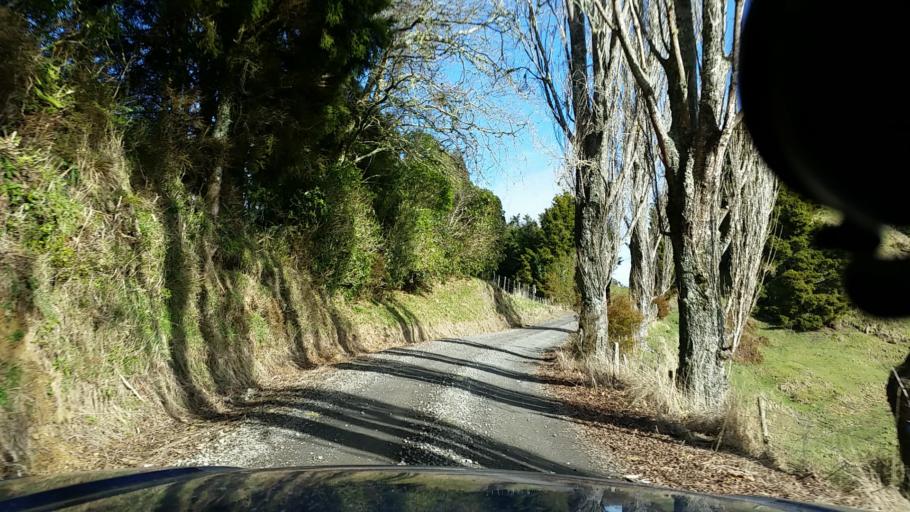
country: NZ
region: Taranaki
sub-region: New Plymouth District
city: Waitara
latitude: -39.0328
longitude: 174.7875
